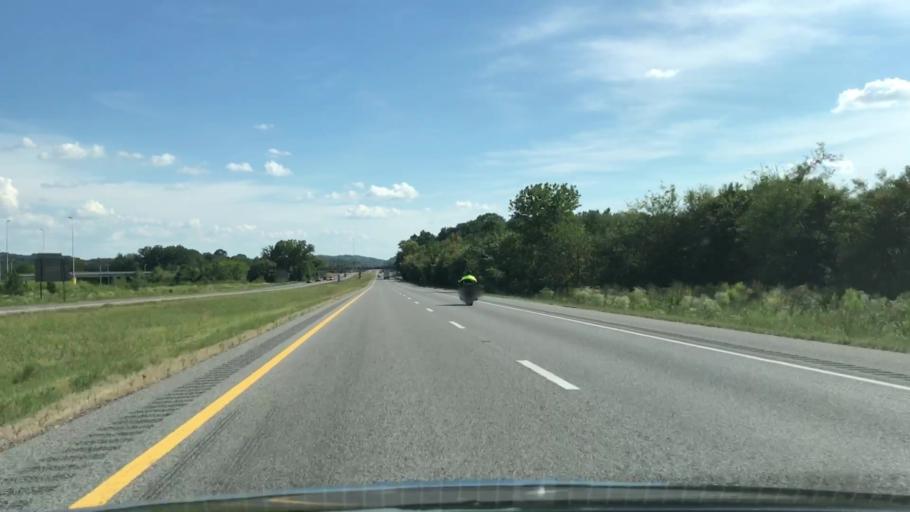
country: US
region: Alabama
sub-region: Limestone County
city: Ardmore
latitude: 35.0666
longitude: -86.8822
